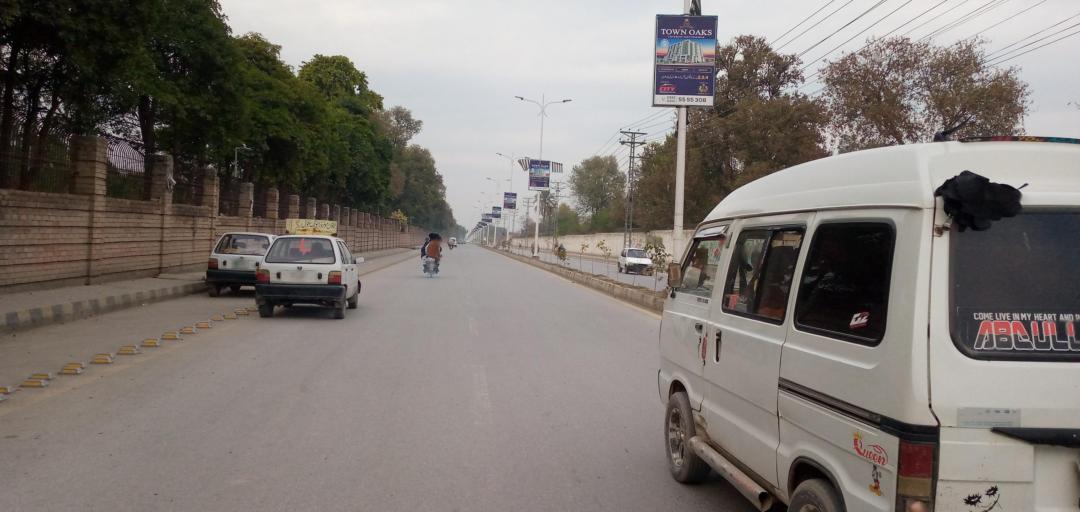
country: PK
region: Khyber Pakhtunkhwa
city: Peshawar
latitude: 33.9997
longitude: 71.4885
